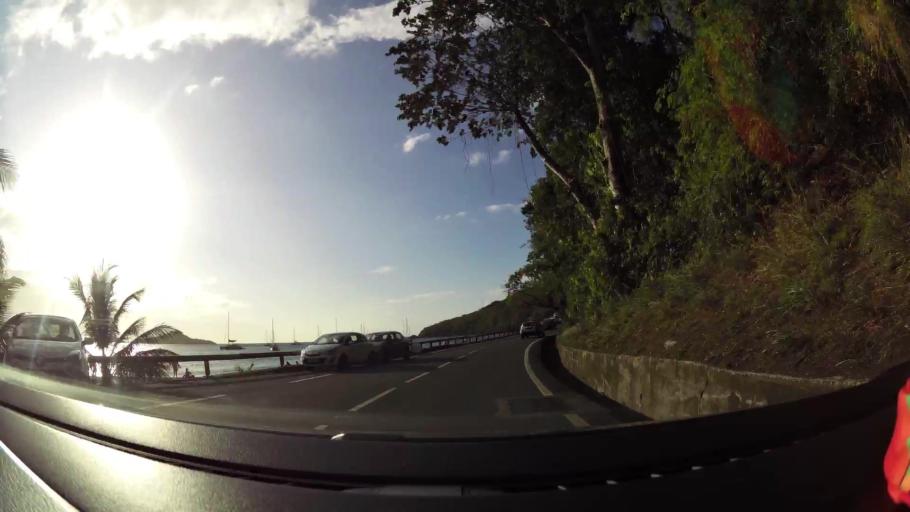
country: GP
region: Guadeloupe
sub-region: Guadeloupe
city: Bouillante
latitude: 16.1730
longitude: -61.7771
